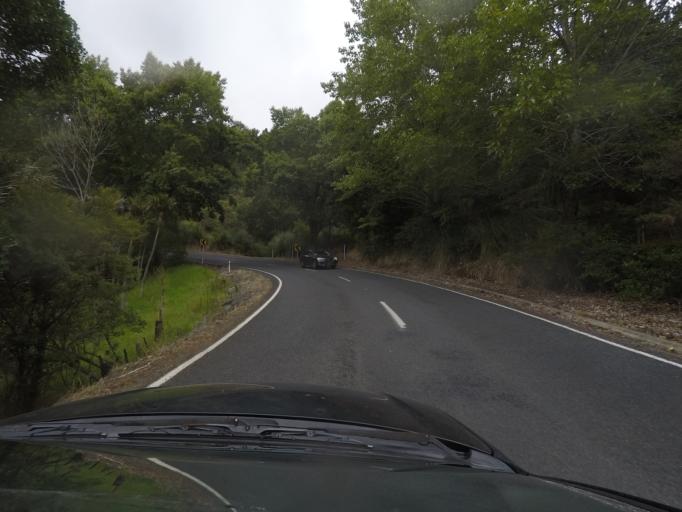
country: NZ
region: Auckland
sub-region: Auckland
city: Warkworth
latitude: -36.2733
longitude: 174.6966
